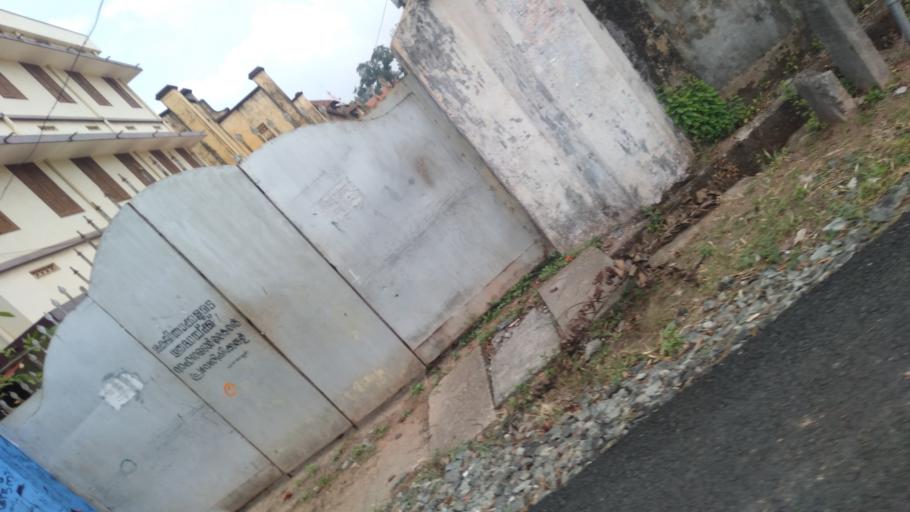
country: IN
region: Kerala
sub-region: Alappuzha
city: Alleppey
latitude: 9.4950
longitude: 76.3280
